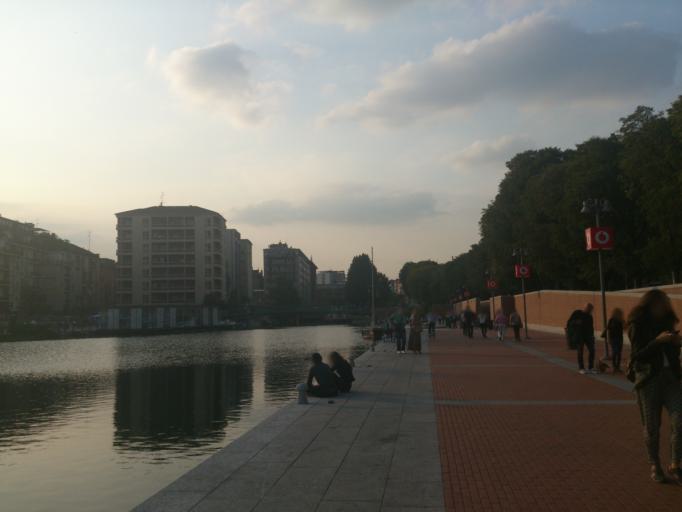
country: IT
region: Lombardy
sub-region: Citta metropolitana di Milano
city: Milano
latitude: 45.4534
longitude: 9.1764
